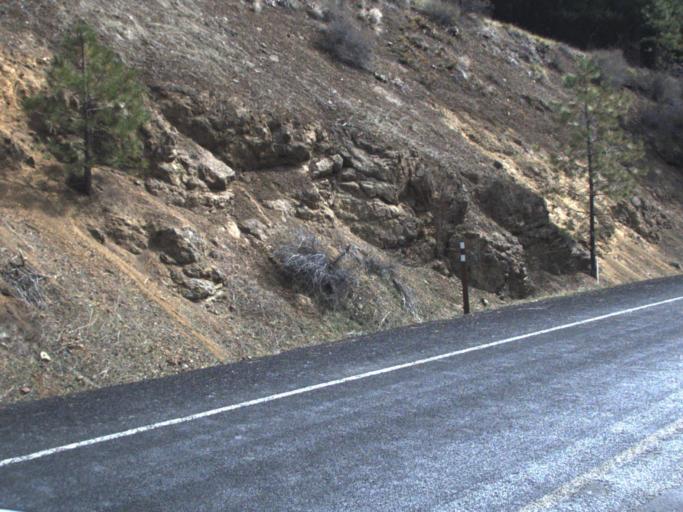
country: US
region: Washington
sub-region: Kittitas County
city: Cle Elum
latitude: 46.9277
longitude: -121.0467
